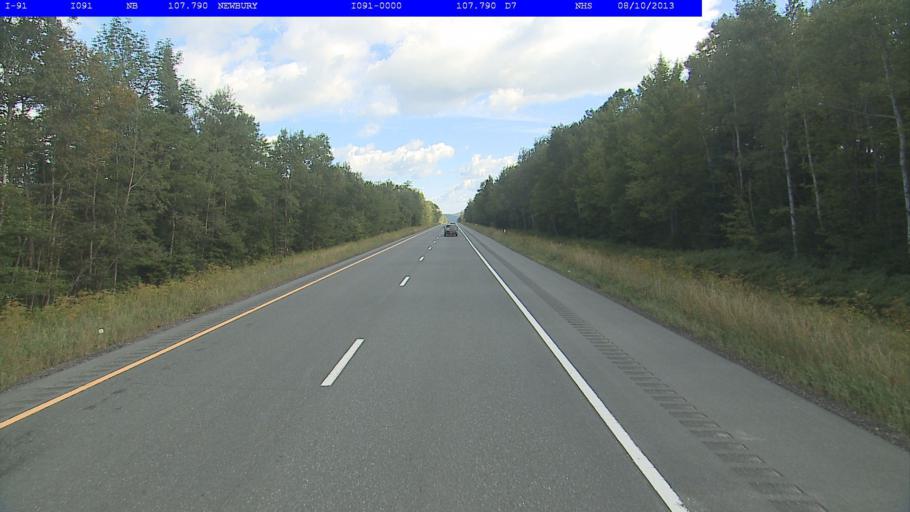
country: US
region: New Hampshire
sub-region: Grafton County
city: Woodsville
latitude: 44.1254
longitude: -72.1039
